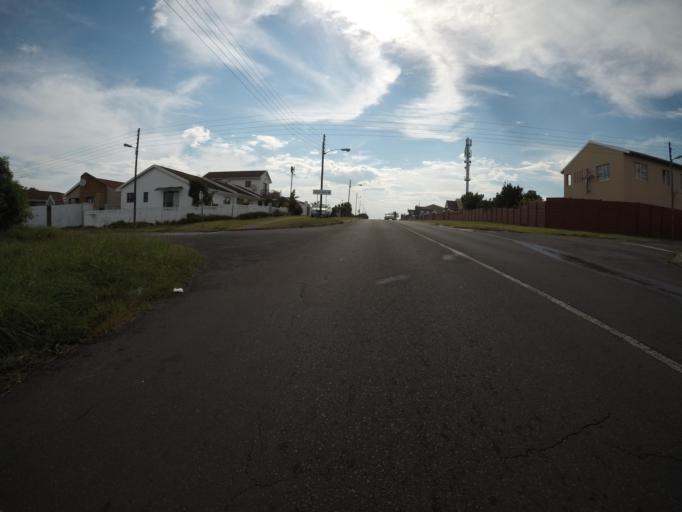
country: ZA
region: Eastern Cape
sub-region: Buffalo City Metropolitan Municipality
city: East London
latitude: -33.0224
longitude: 27.8734
